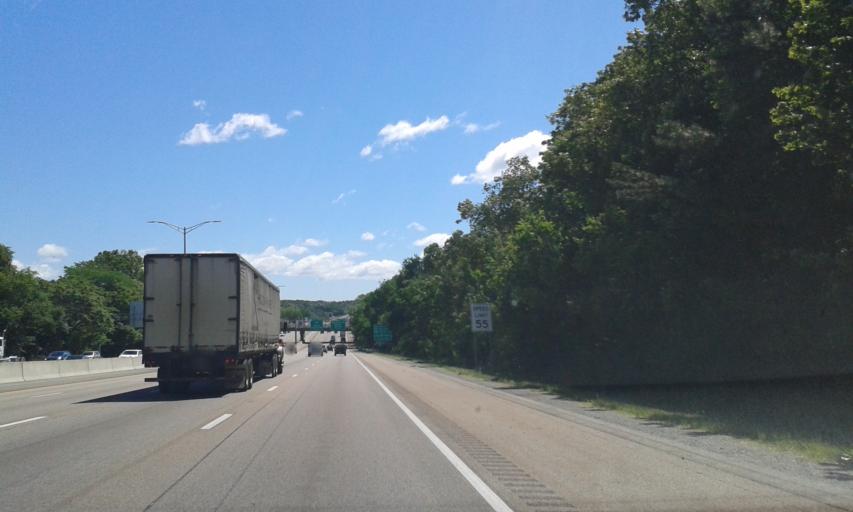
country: US
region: Massachusetts
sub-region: Middlesex County
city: Woburn
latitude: 42.5007
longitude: -71.1466
